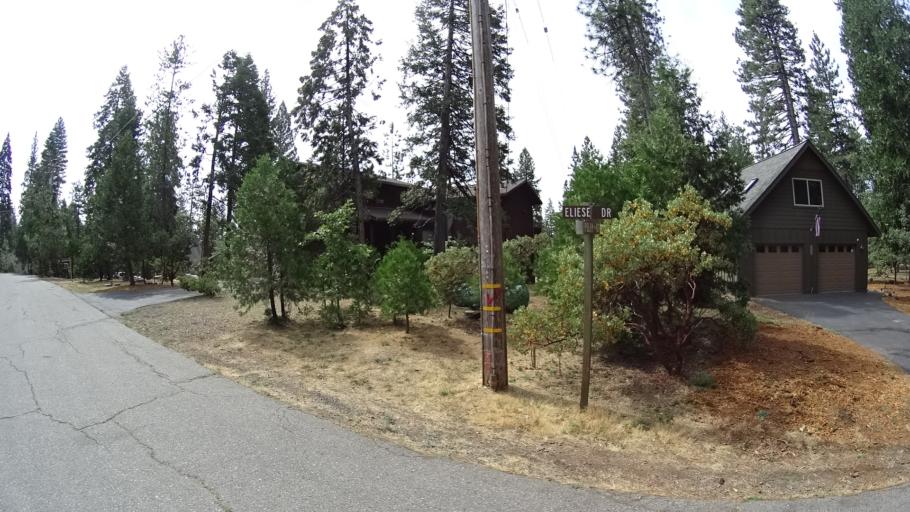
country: US
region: California
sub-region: Calaveras County
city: Arnold
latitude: 38.2453
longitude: -120.3522
